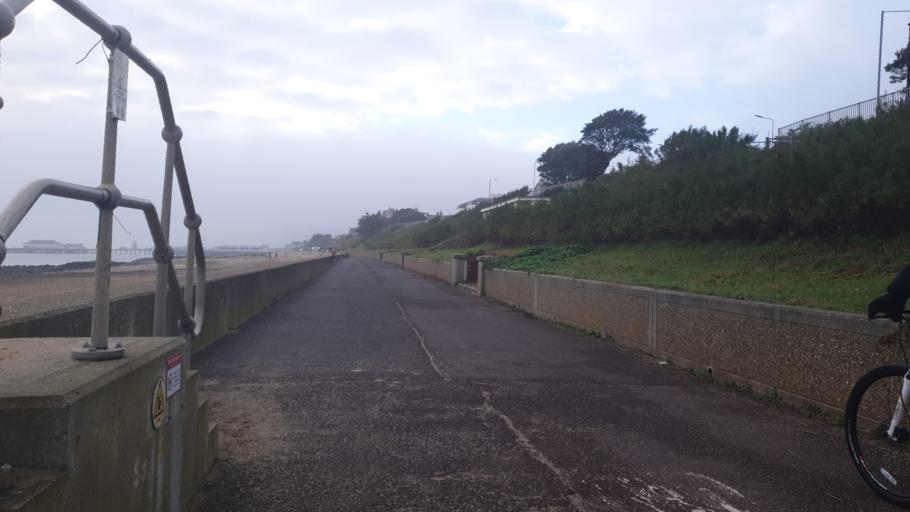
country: GB
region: England
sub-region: Essex
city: Clacton-on-Sea
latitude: 51.7921
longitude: 1.1675
